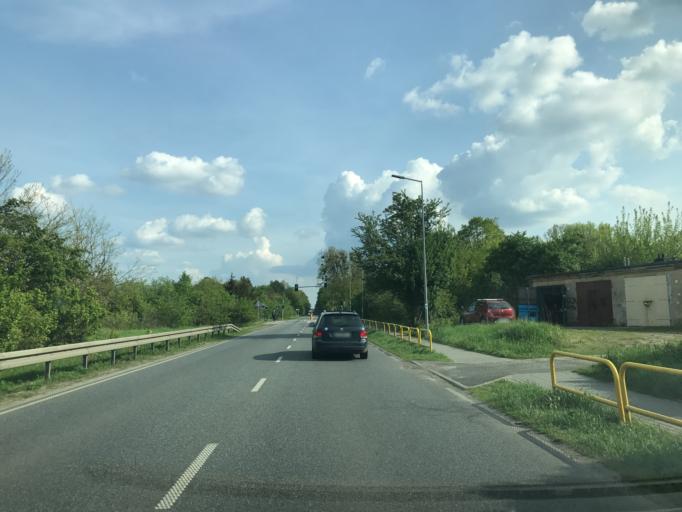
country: PL
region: Kujawsko-Pomorskie
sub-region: Bydgoszcz
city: Fordon
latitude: 53.0936
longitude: 18.1125
